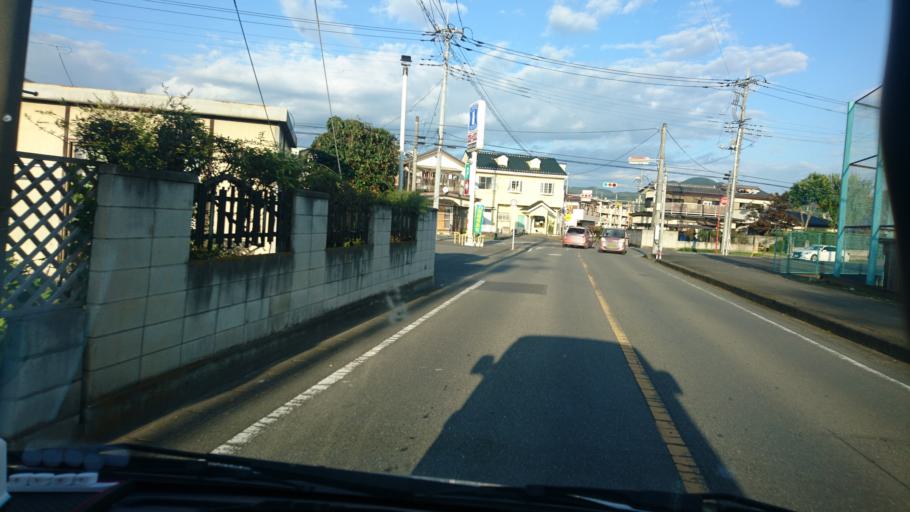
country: JP
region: Gunma
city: Omamacho-omama
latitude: 36.4230
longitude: 139.2906
